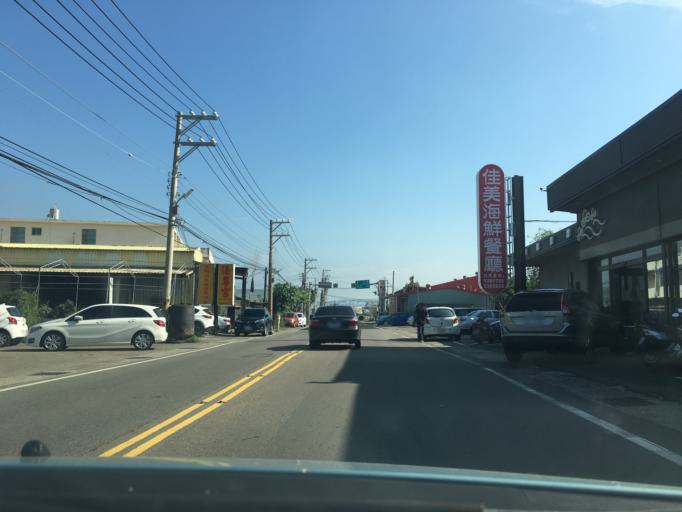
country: TW
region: Taiwan
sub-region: Hsinchu
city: Hsinchu
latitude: 24.8058
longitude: 120.9220
